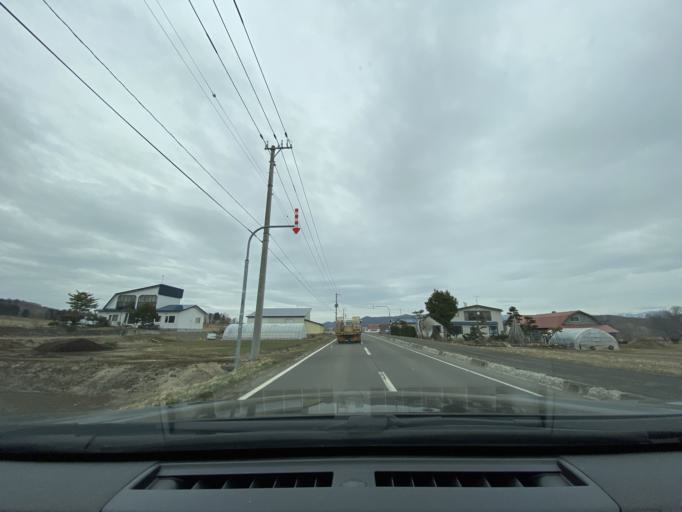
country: JP
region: Hokkaido
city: Nayoro
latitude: 44.0994
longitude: 142.4753
